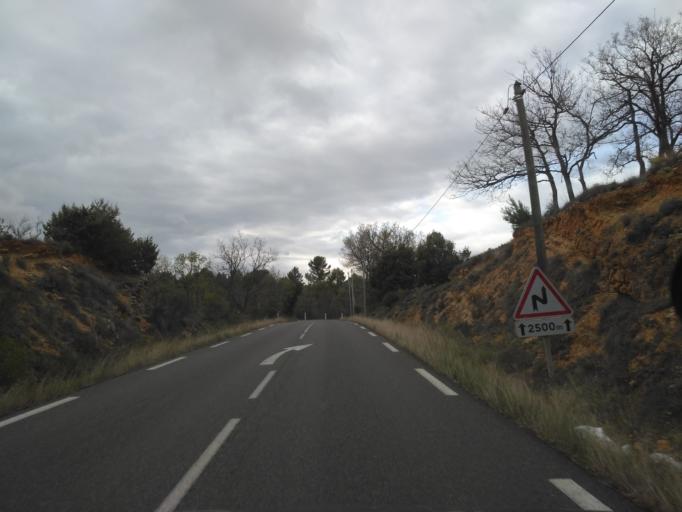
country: FR
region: Provence-Alpes-Cote d'Azur
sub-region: Departement du Var
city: Saint-Julien
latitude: 43.6226
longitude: 5.9439
